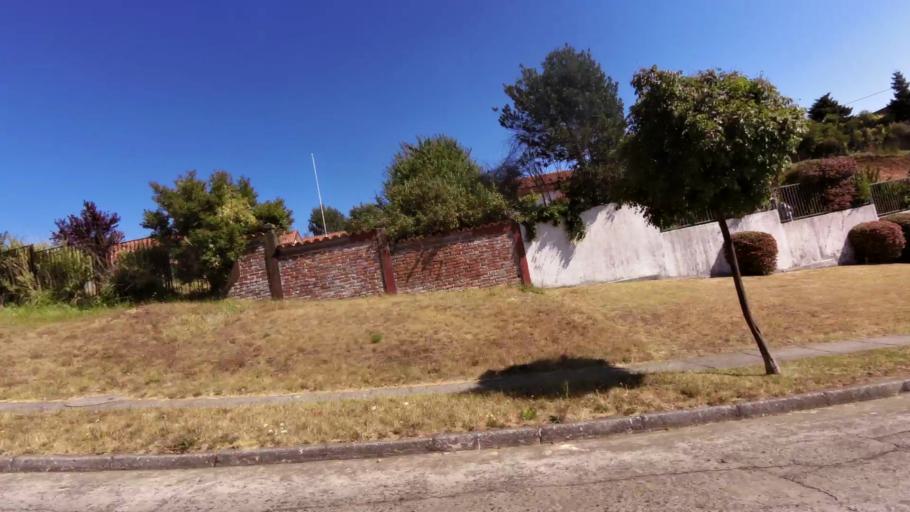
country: CL
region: Biobio
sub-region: Provincia de Concepcion
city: Concepcion
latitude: -36.7921
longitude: -73.0542
